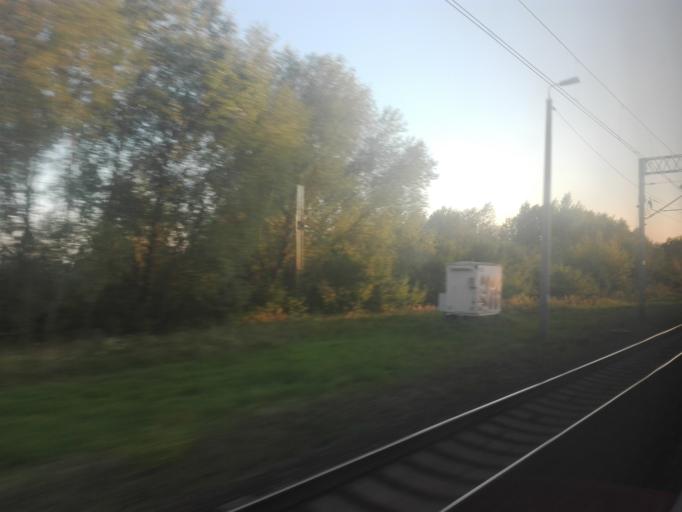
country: PL
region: Masovian Voivodeship
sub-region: Powiat warszawski zachodni
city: Blonie
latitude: 52.1864
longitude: 20.5932
